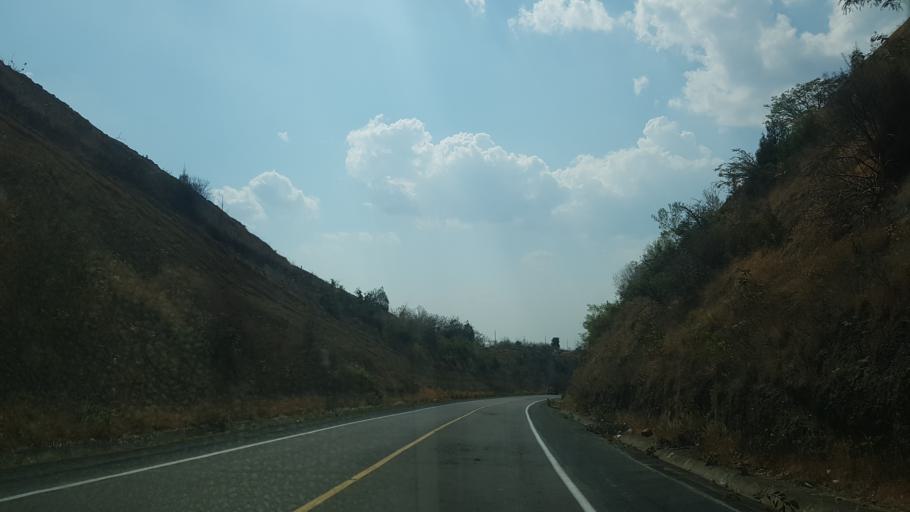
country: MX
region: Puebla
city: San Juan Amecac
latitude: 18.8156
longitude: -98.6749
